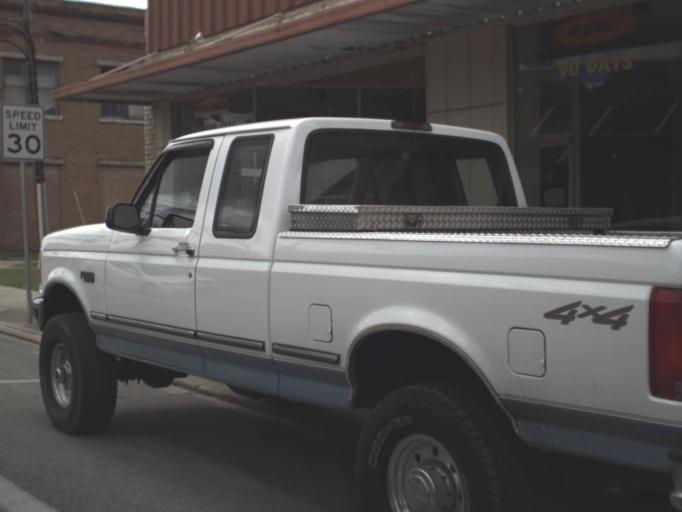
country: US
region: Florida
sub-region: Hamilton County
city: Jasper
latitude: 30.5183
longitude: -82.9488
